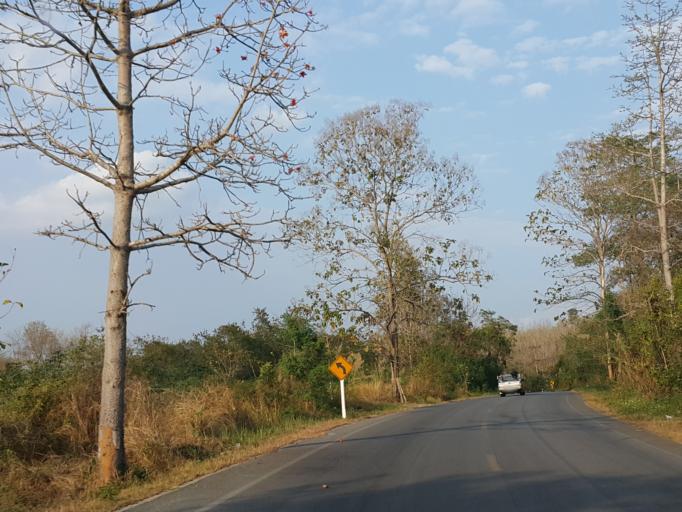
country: TH
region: Lampang
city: Lampang
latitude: 18.4540
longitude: 99.4561
